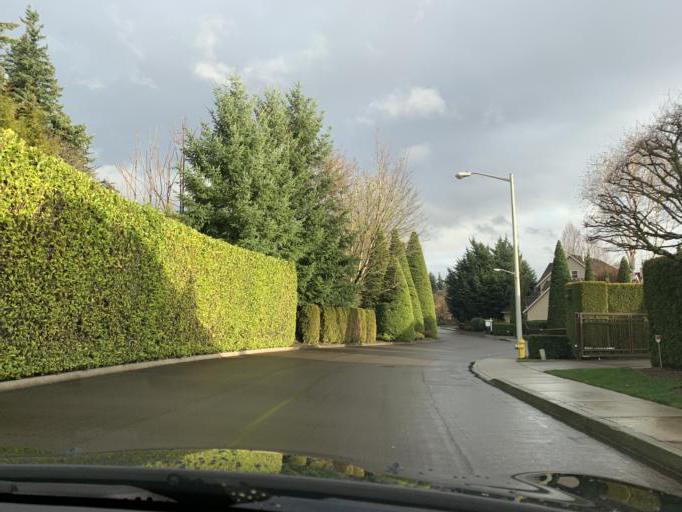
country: US
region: Washington
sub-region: Clark County
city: Mill Plain
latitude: 45.5895
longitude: -122.5106
